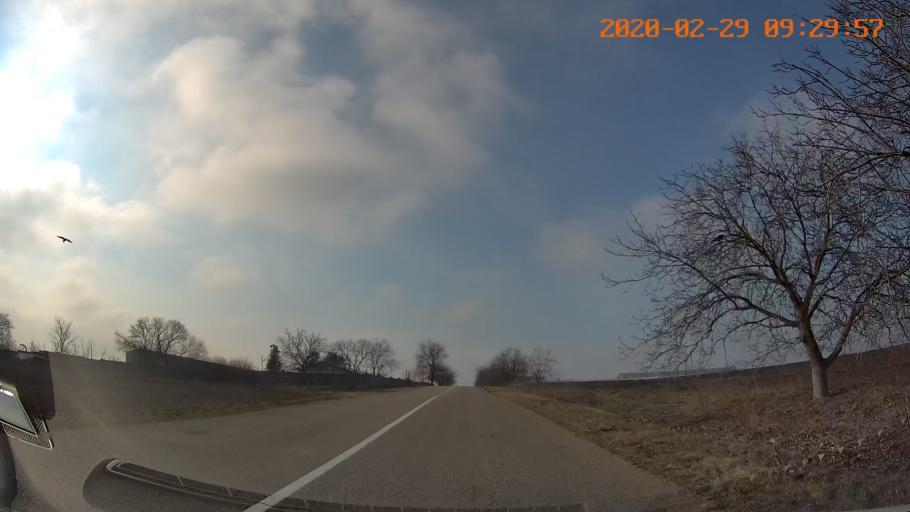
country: UA
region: Odessa
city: Lymanske
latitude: 46.6721
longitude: 29.9187
